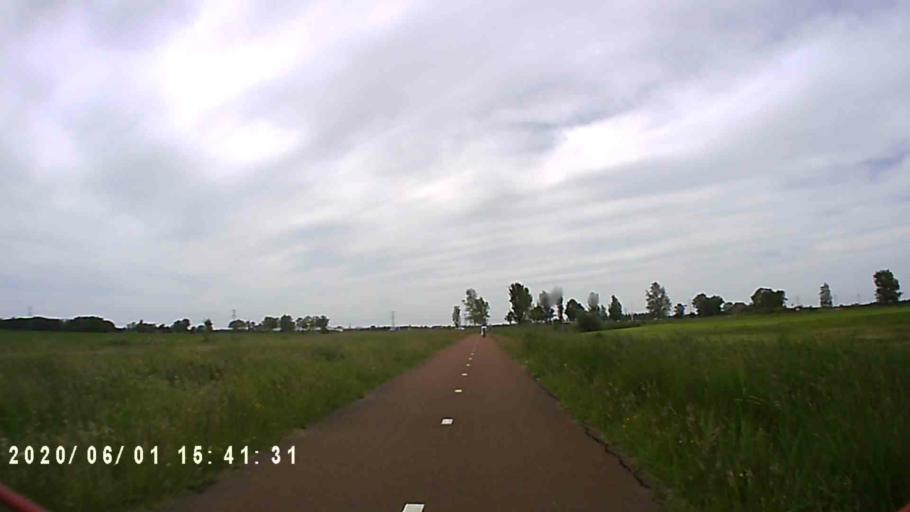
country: NL
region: Friesland
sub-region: Gemeente Boarnsterhim
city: Wergea
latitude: 53.1563
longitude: 5.8249
